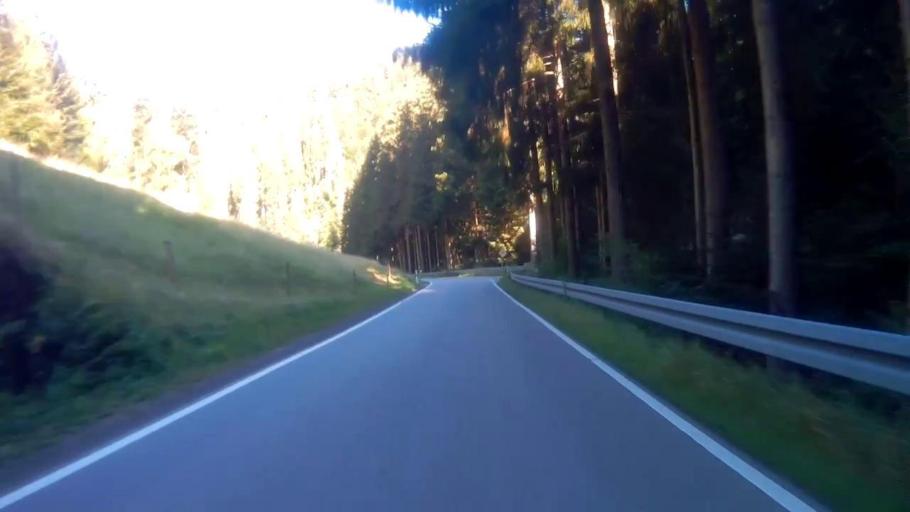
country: DE
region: Baden-Wuerttemberg
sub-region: Freiburg Region
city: Horben
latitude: 47.8893
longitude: 7.8536
